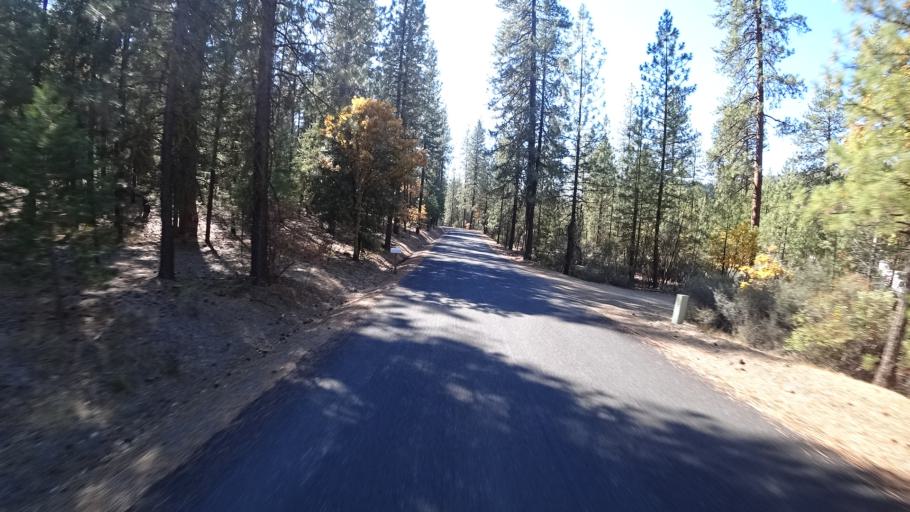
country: US
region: California
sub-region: Siskiyou County
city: Yreka
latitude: 41.6544
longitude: -122.8595
